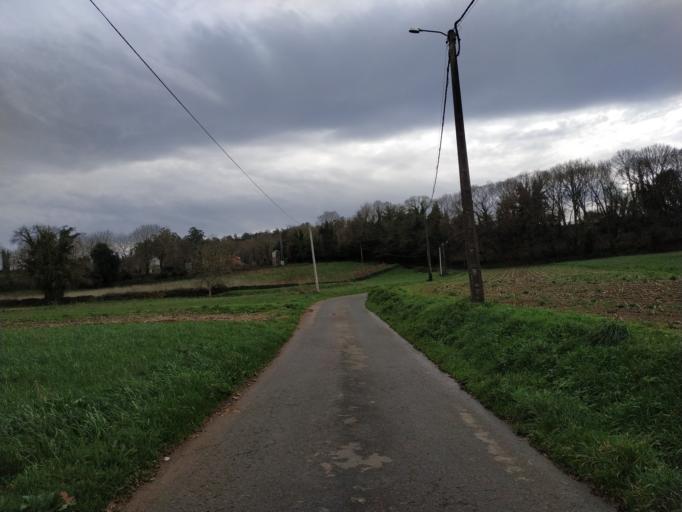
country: ES
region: Galicia
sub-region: Provincia de Pontevedra
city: Silleda
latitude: 42.7803
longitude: -8.1712
